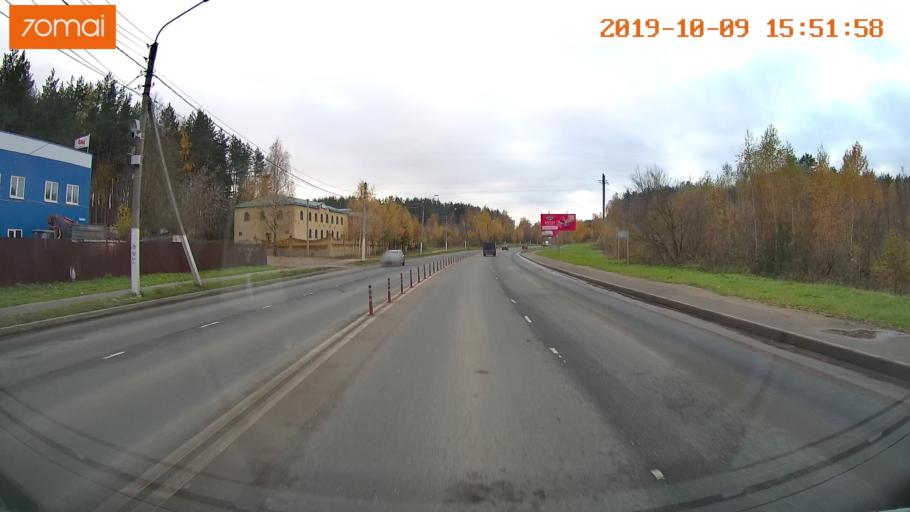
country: RU
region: Kostroma
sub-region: Kostromskoy Rayon
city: Kostroma
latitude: 57.7933
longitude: 40.9740
